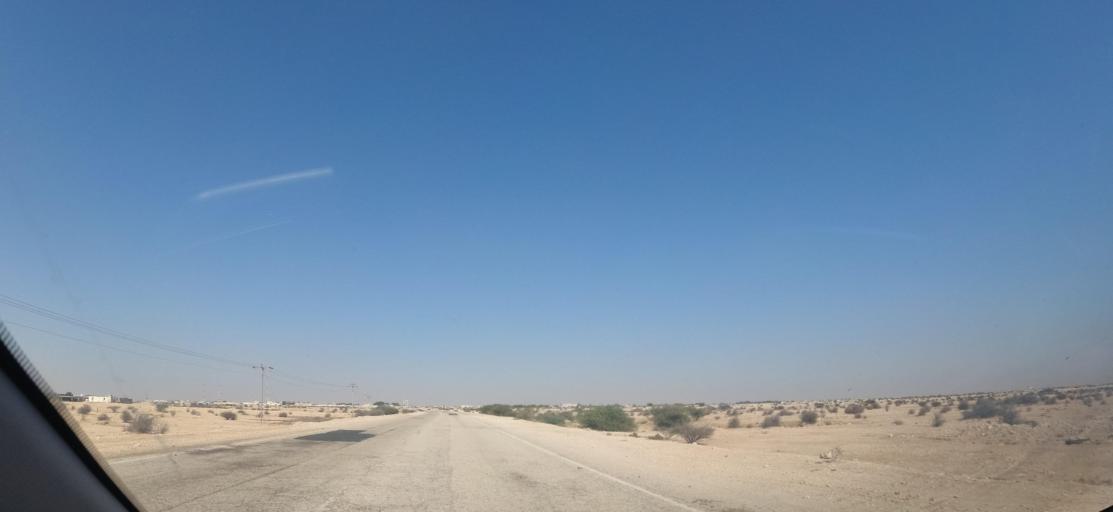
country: QA
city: Al Jumayliyah
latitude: 25.6036
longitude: 51.0742
